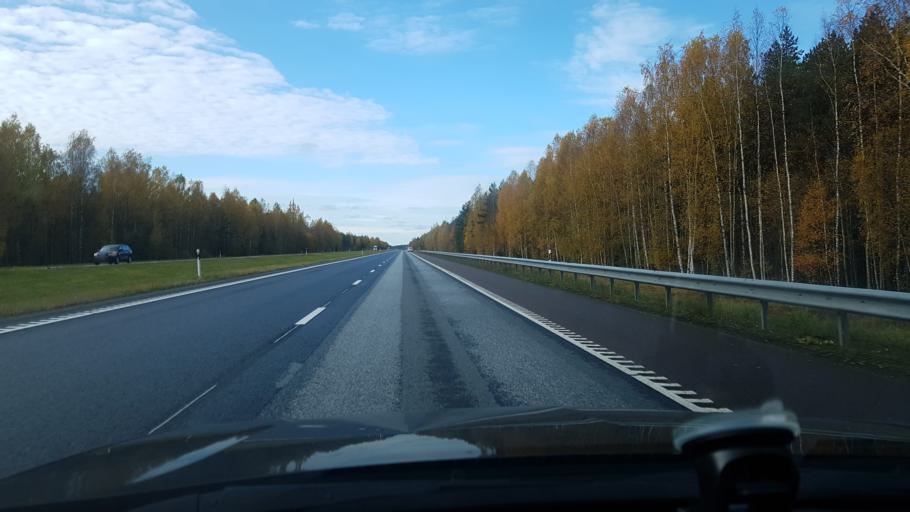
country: EE
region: Harju
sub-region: Kuusalu vald
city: Kuusalu
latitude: 59.4594
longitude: 25.5720
